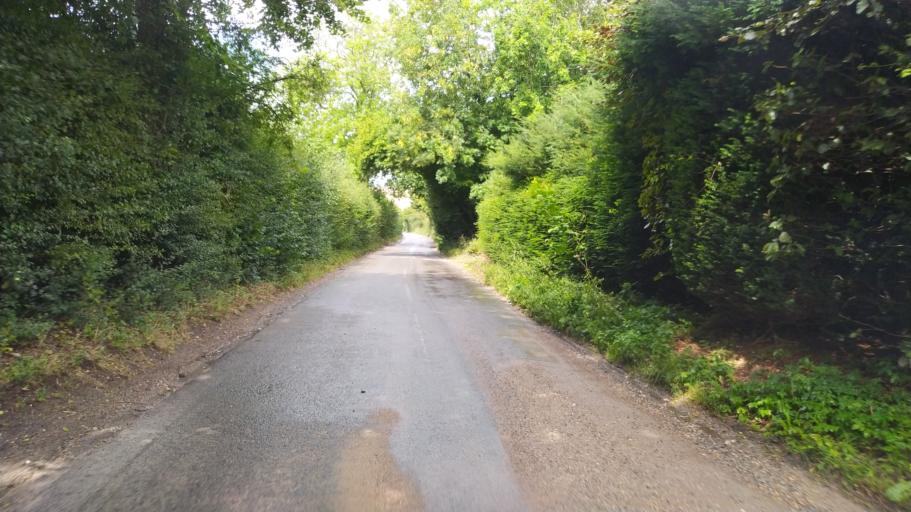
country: GB
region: England
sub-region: Hampshire
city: Swanmore
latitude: 51.0082
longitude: -1.1304
